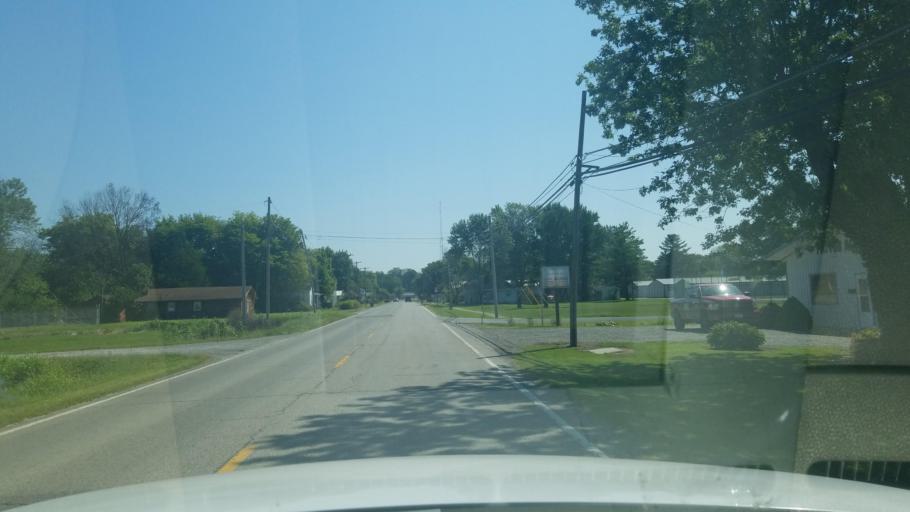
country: US
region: Illinois
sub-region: Saline County
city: Harrisburg
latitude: 37.7388
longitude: -88.5552
